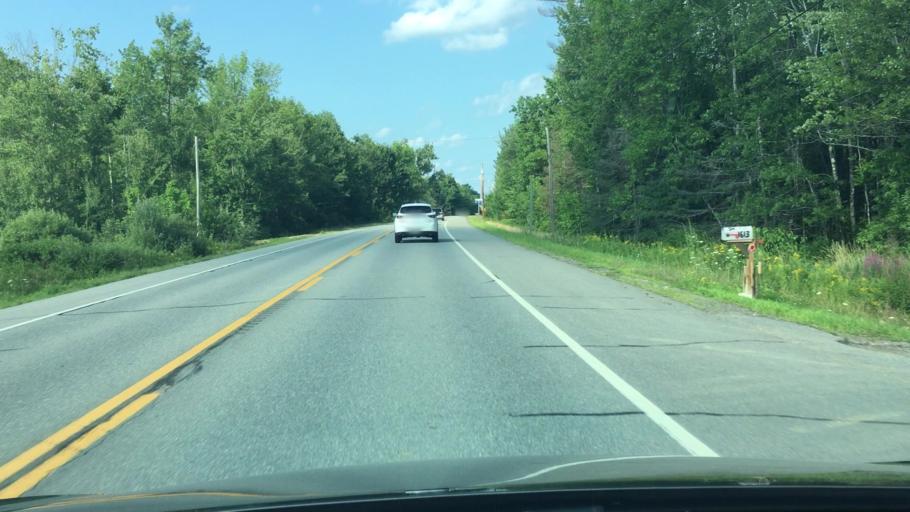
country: US
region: Maine
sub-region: Kennebec County
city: Windsor
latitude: 44.3728
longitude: -69.6285
